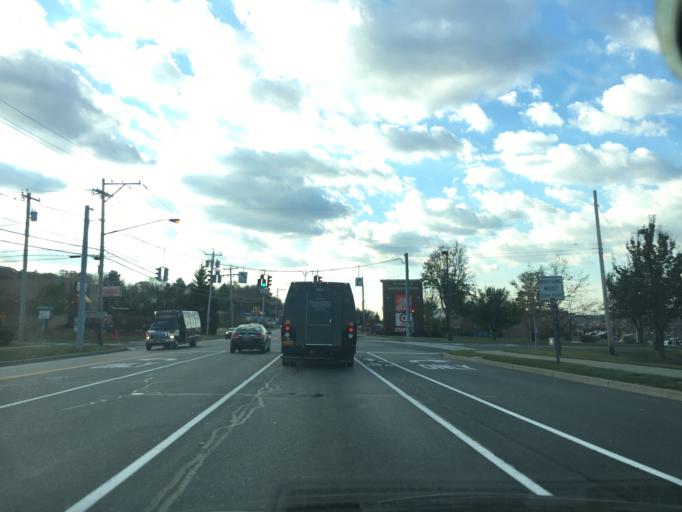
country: US
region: New York
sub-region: Rensselaer County
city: Hampton Manor
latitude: 42.6466
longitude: -73.6978
